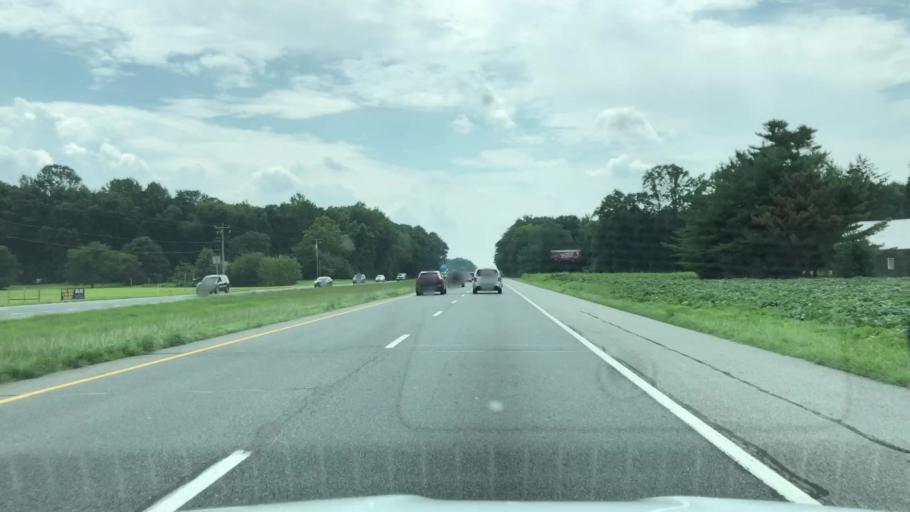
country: US
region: Delaware
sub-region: Kent County
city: Woodside East
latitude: 39.0804
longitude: -75.5520
